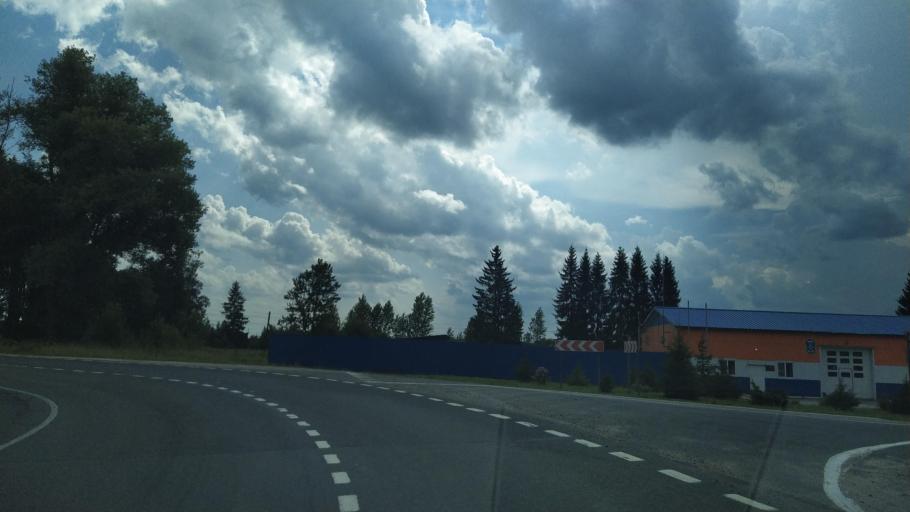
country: RU
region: Pskov
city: Pskov
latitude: 57.7625
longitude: 28.7546
